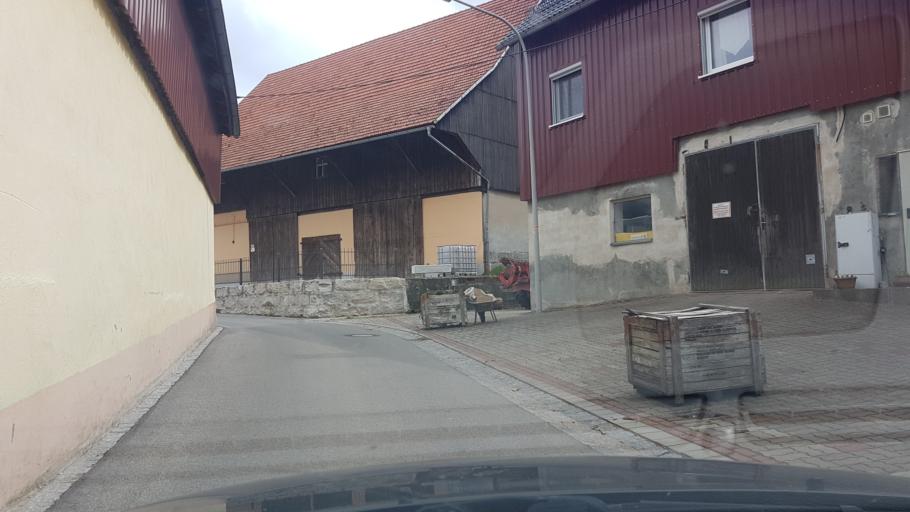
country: DE
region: Bavaria
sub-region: Upper Franconia
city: Wattendorf
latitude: 50.0058
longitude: 11.1539
